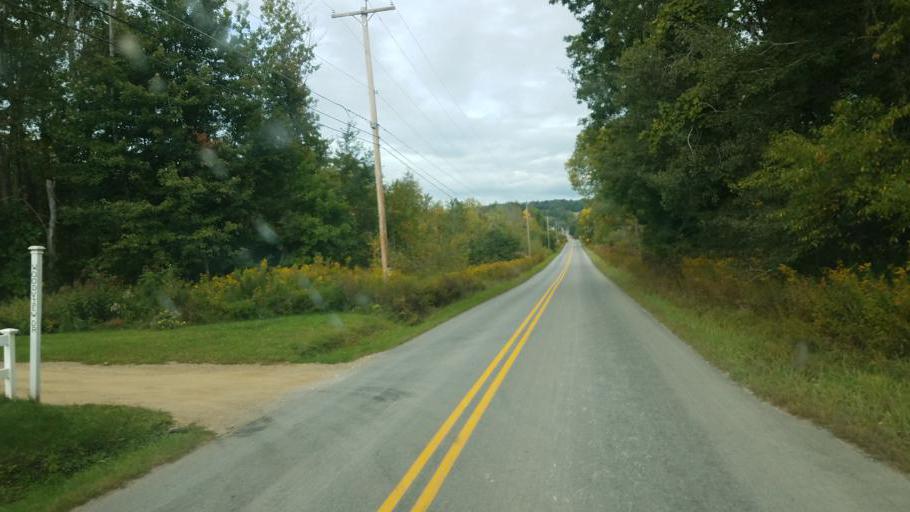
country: US
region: Pennsylvania
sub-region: Mercer County
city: Greenville
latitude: 41.5054
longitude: -80.3544
